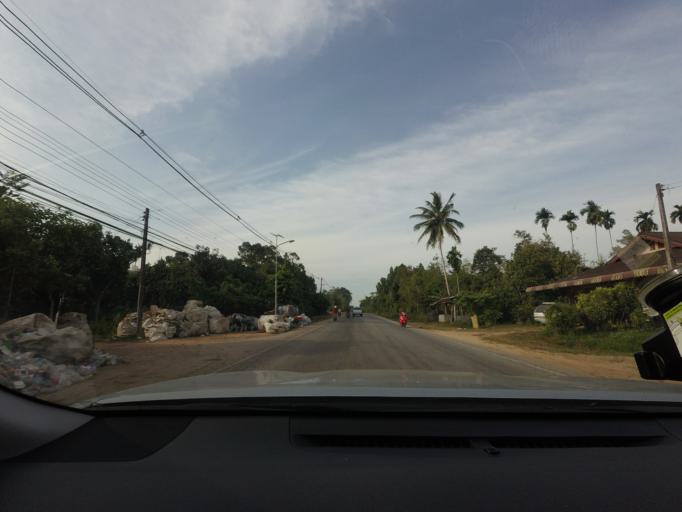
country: TH
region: Narathiwat
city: Ra-ngae
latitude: 6.3044
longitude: 101.7276
